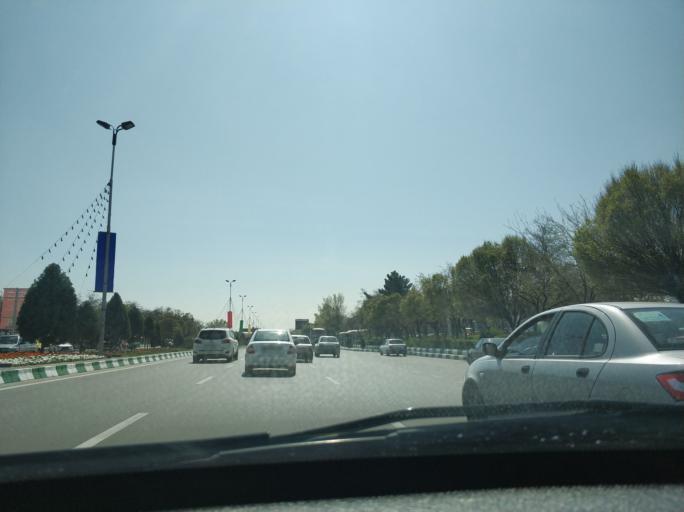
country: IR
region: Razavi Khorasan
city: Mashhad
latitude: 36.2575
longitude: 59.6092
